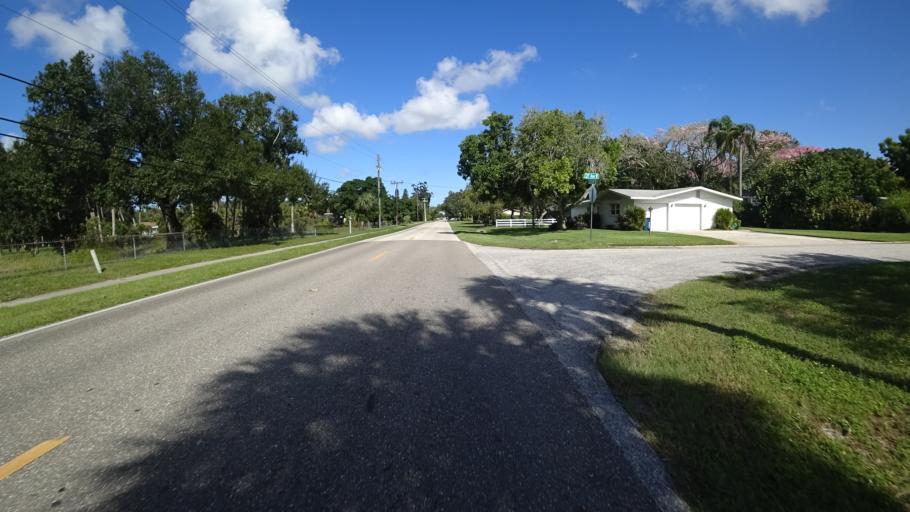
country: US
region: Florida
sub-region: Manatee County
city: West Bradenton
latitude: 27.4763
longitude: -82.6122
